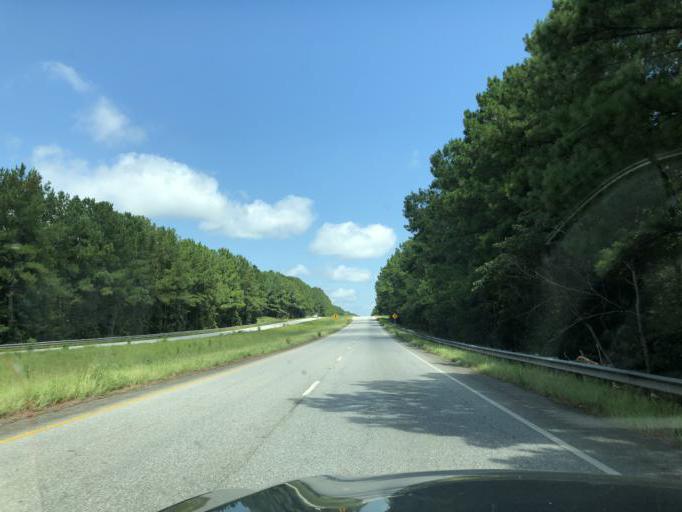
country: US
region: Alabama
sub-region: Henry County
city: Abbeville
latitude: 31.6512
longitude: -85.2803
